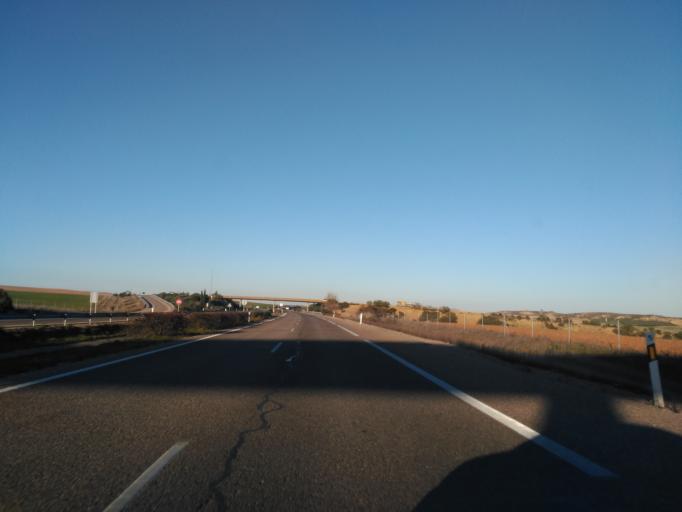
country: ES
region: Castille and Leon
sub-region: Provincia de Zamora
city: Canizal
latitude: 41.1715
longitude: -5.3765
